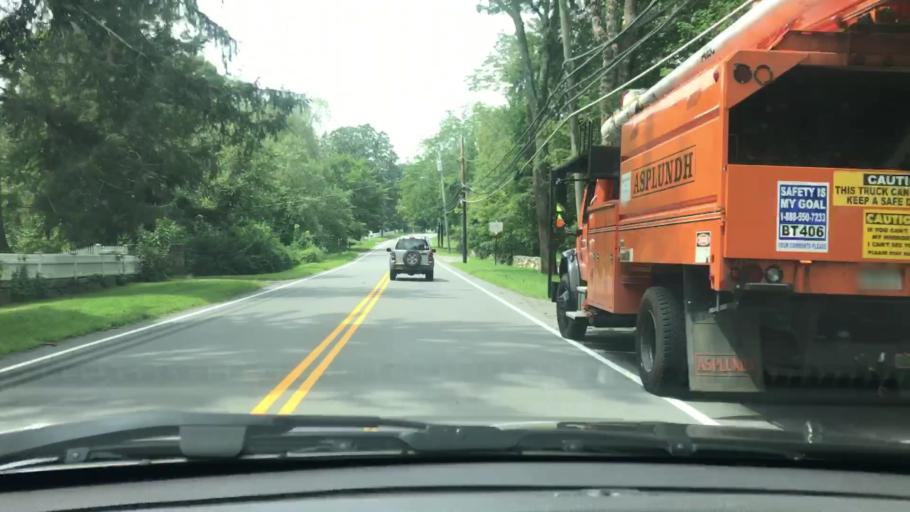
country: US
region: New York
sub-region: Westchester County
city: Bedford
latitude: 41.2025
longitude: -73.6371
